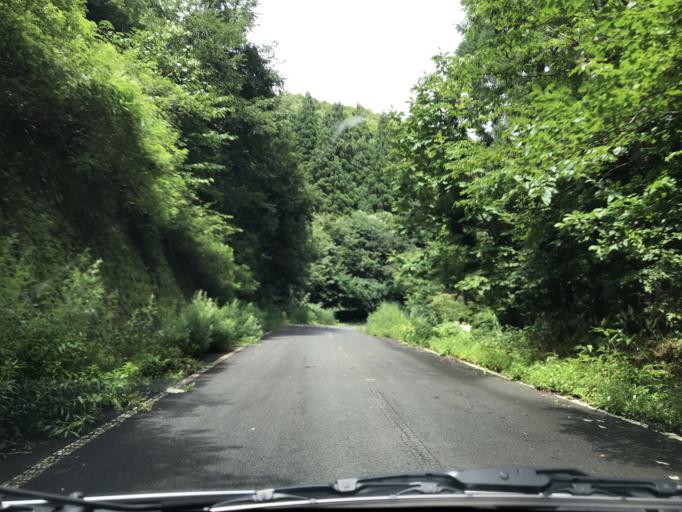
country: JP
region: Iwate
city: Tono
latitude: 39.0921
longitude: 141.4141
